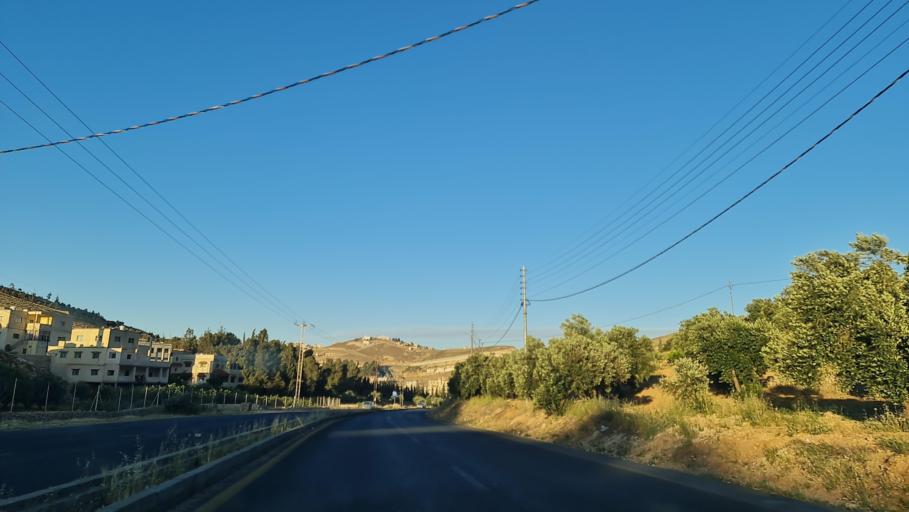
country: JO
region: Amman
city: Al Jubayhah
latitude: 32.0921
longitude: 35.9448
